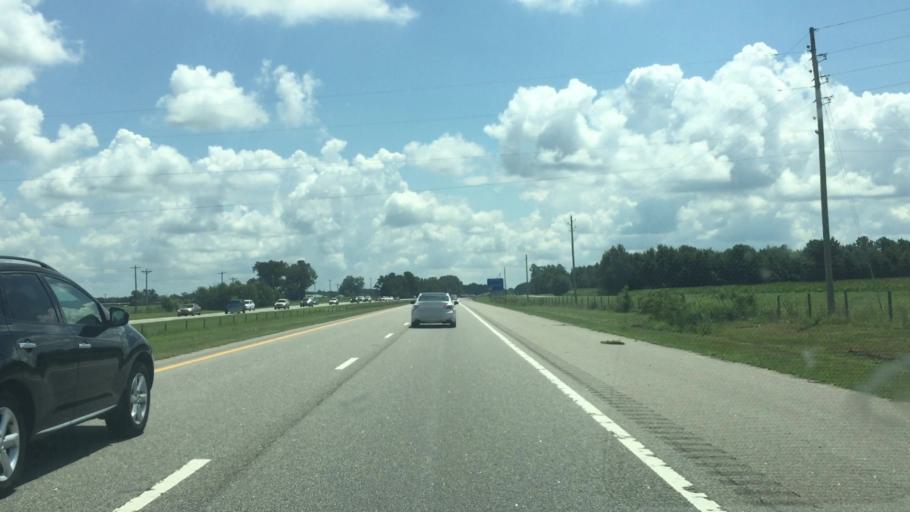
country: US
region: North Carolina
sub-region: Robeson County
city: Lumberton
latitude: 34.5881
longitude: -79.0645
